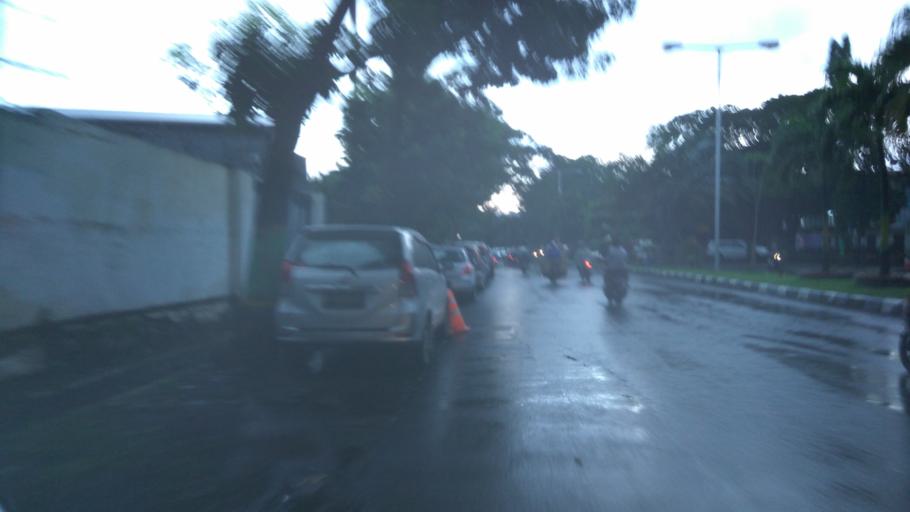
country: ID
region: Central Java
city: Semarang
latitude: -6.9869
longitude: 110.3860
